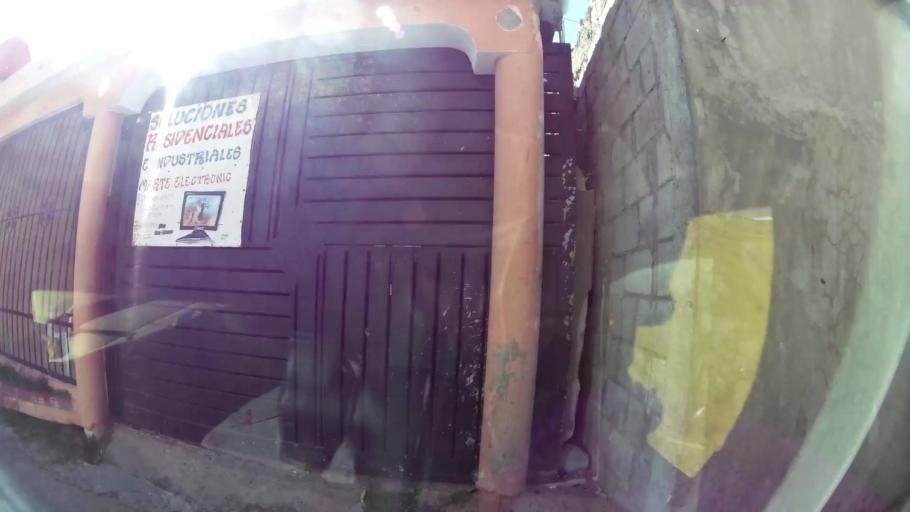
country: DO
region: San Cristobal
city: San Cristobal
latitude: 18.4311
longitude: -70.1211
